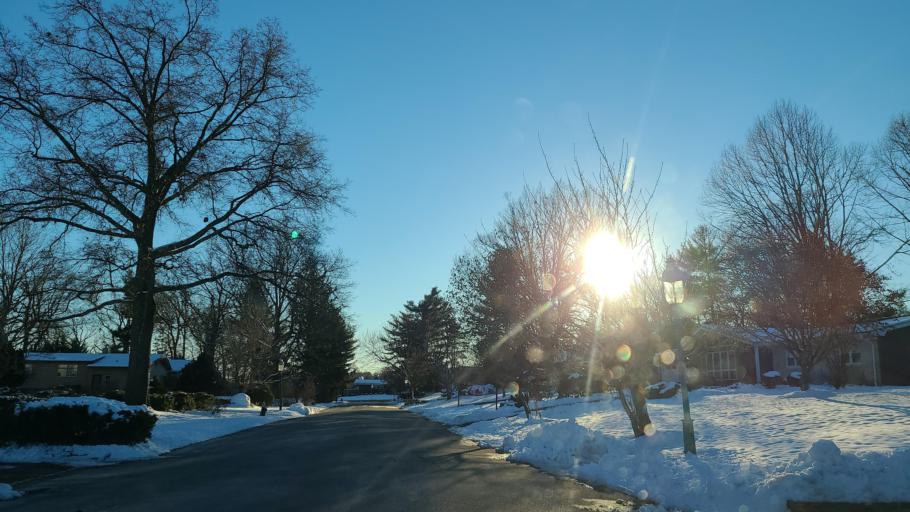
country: US
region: New Jersey
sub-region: Essex County
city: South Orange
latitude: 40.7583
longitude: -74.2708
